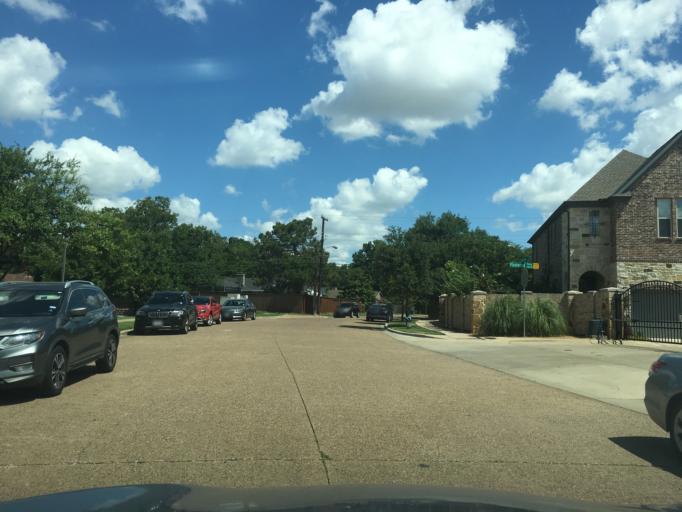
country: US
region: Texas
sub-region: Dallas County
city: Garland
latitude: 32.8665
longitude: -96.7039
